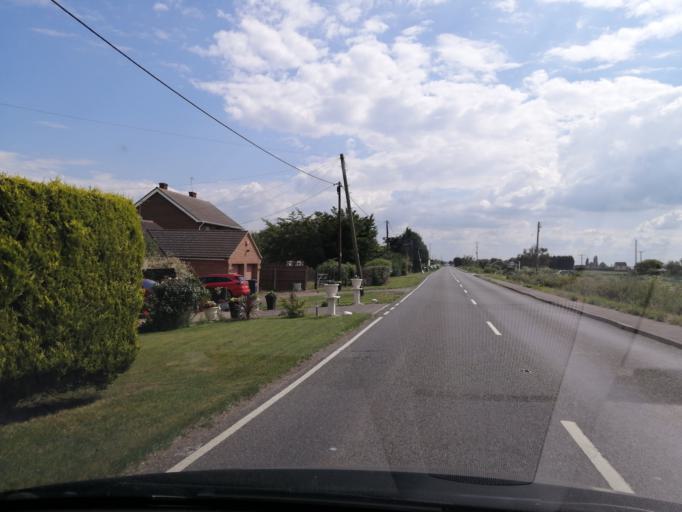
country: GB
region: England
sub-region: Cambridgeshire
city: Ramsey
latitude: 52.4900
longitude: -0.1486
